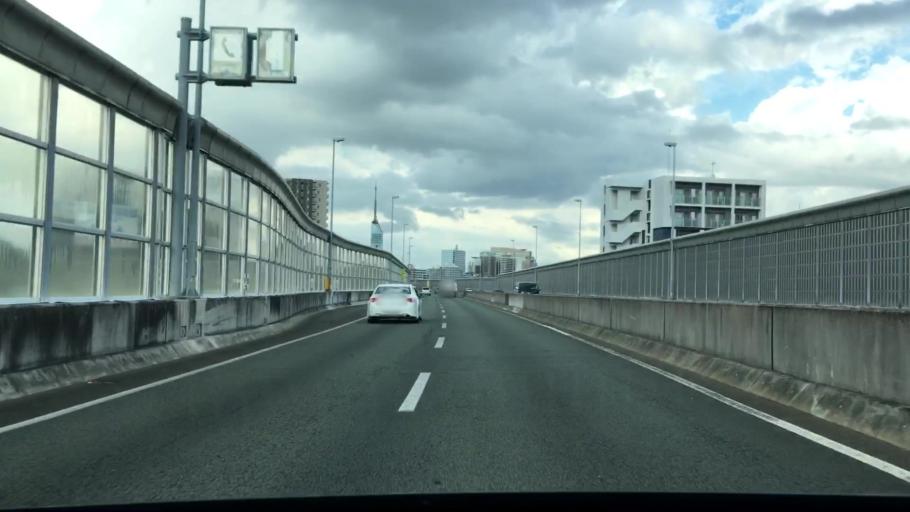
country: JP
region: Fukuoka
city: Fukuoka-shi
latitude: 33.5819
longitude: 130.3370
